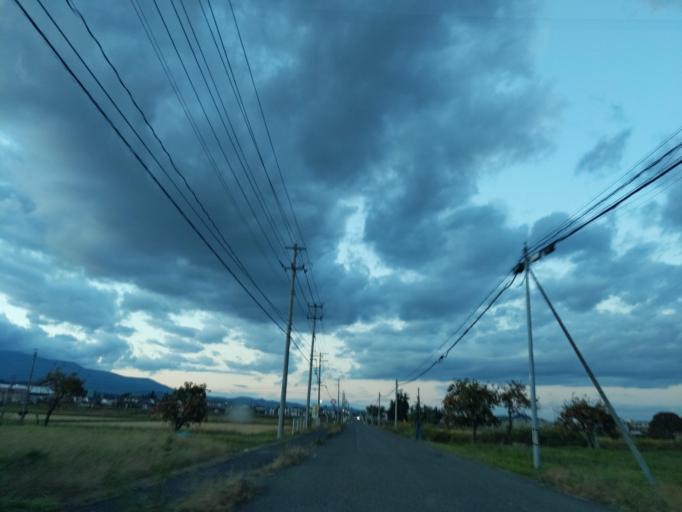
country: JP
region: Fukushima
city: Motomiya
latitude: 37.4896
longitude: 140.3892
